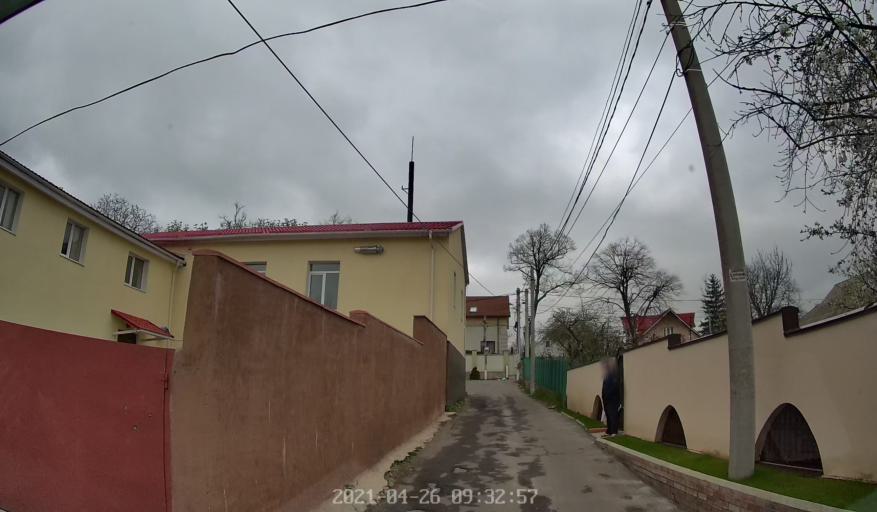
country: MD
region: Chisinau
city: Stauceni
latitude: 47.0920
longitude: 28.8684
